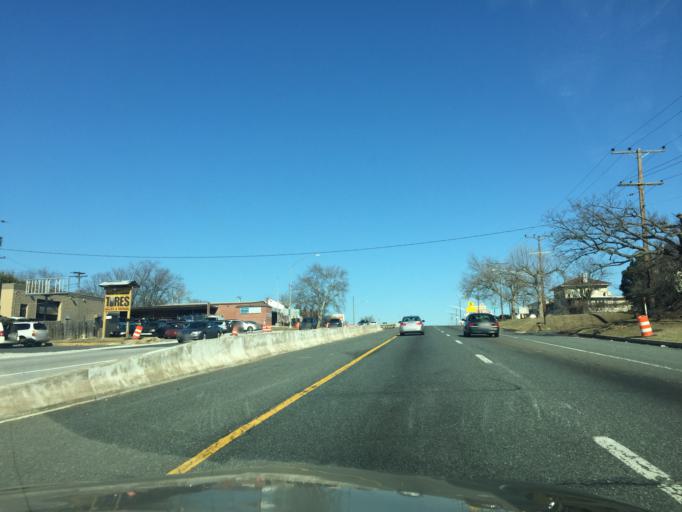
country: US
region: Maryland
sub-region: Baltimore County
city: Rosedale
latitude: 39.3201
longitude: -76.5091
